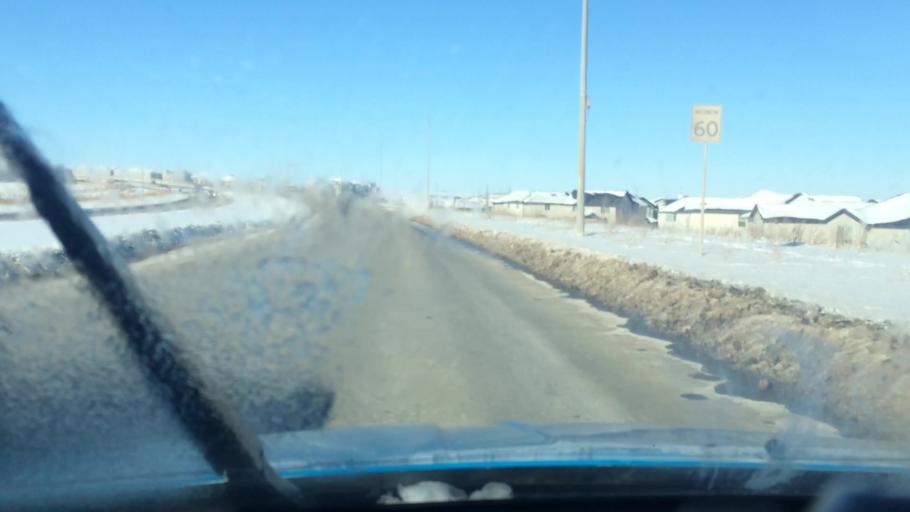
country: CA
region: Alberta
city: Calgary
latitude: 51.1580
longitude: -114.1414
